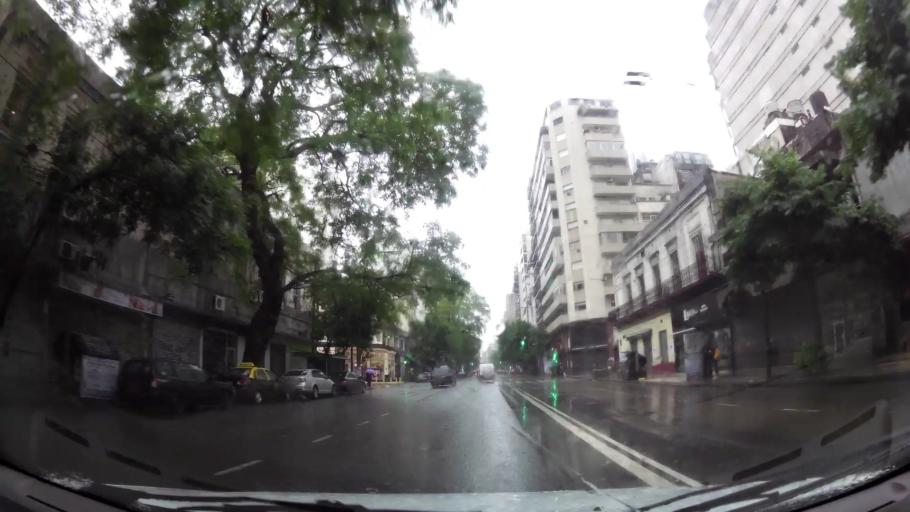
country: AR
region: Buenos Aires F.D.
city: Buenos Aires
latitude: -34.6130
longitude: -58.3918
